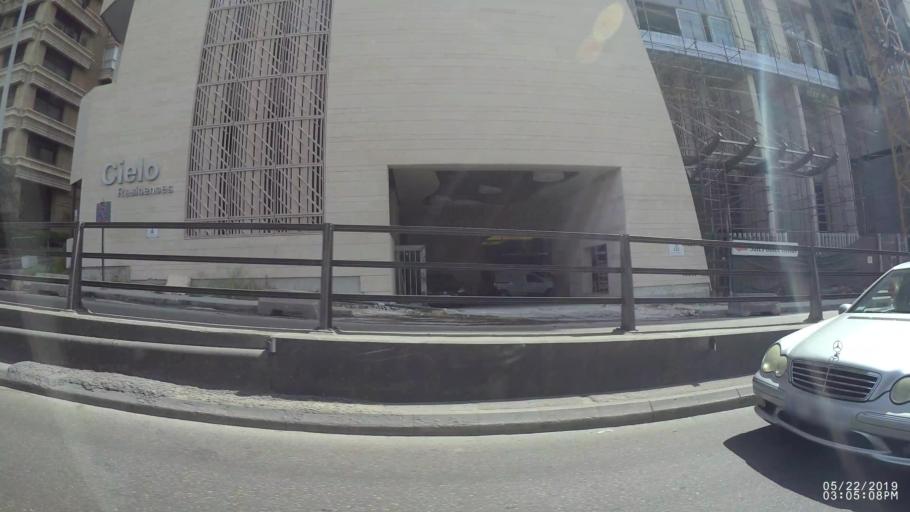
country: LB
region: Beyrouth
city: Beirut
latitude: 33.8949
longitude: 35.4969
